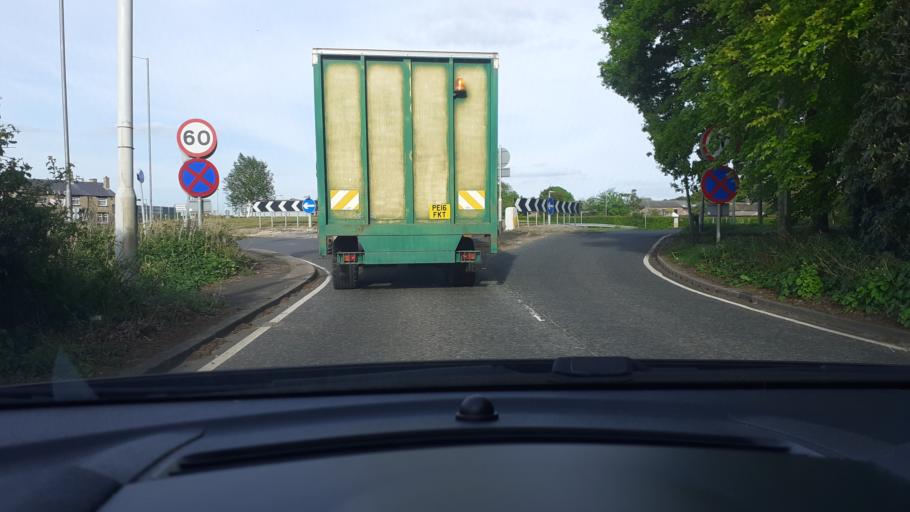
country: GB
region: England
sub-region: St. Helens
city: Rainford
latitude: 53.5161
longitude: -2.8065
